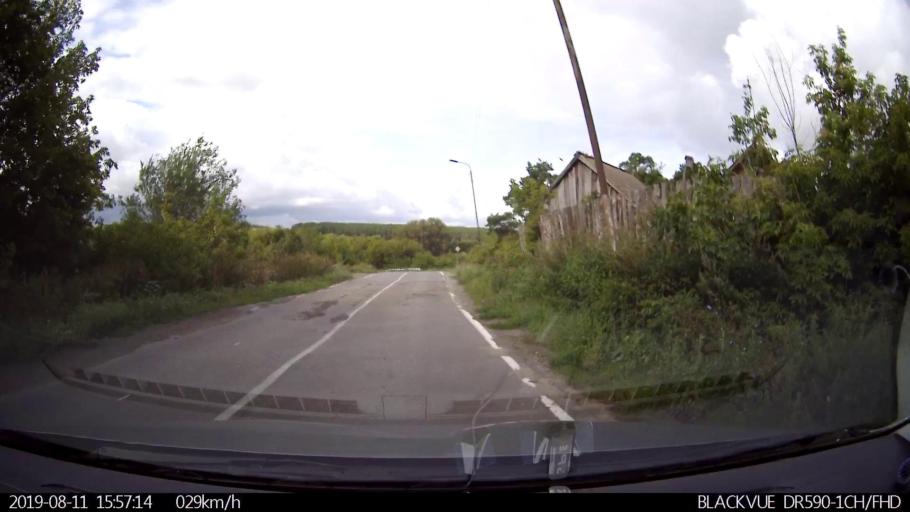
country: RU
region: Ulyanovsk
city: Ignatovka
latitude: 53.9503
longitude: 47.6525
